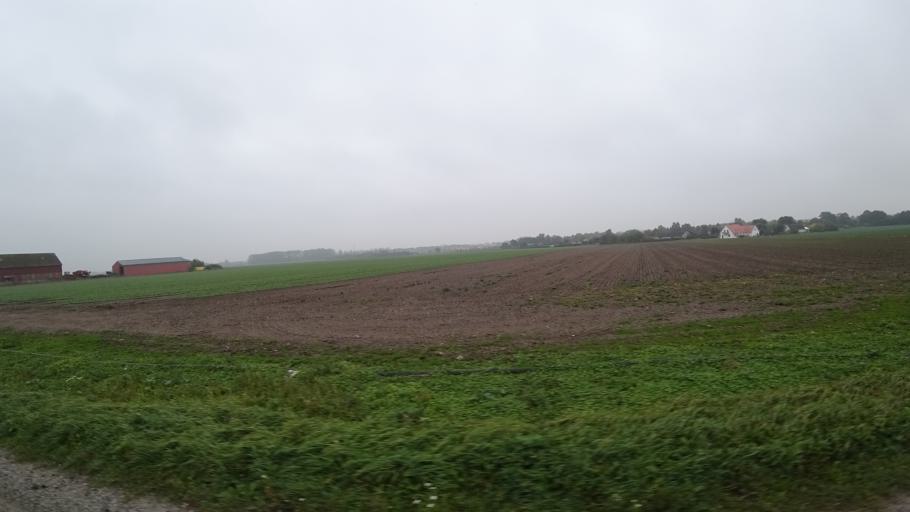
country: SE
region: Skane
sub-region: Kavlinge Kommun
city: Kaevlinge
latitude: 55.8099
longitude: 13.1169
